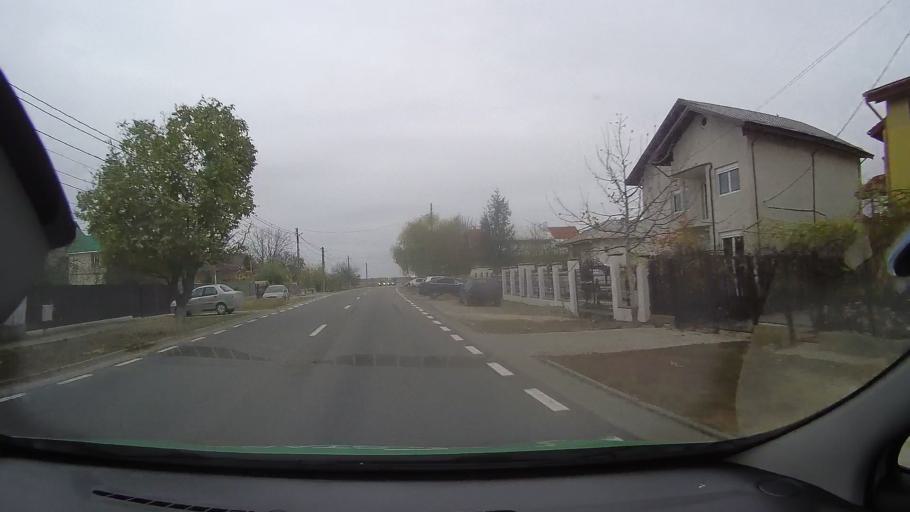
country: RO
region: Ialomita
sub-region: Comuna Slobozia
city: Slobozia
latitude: 44.5967
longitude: 27.3903
